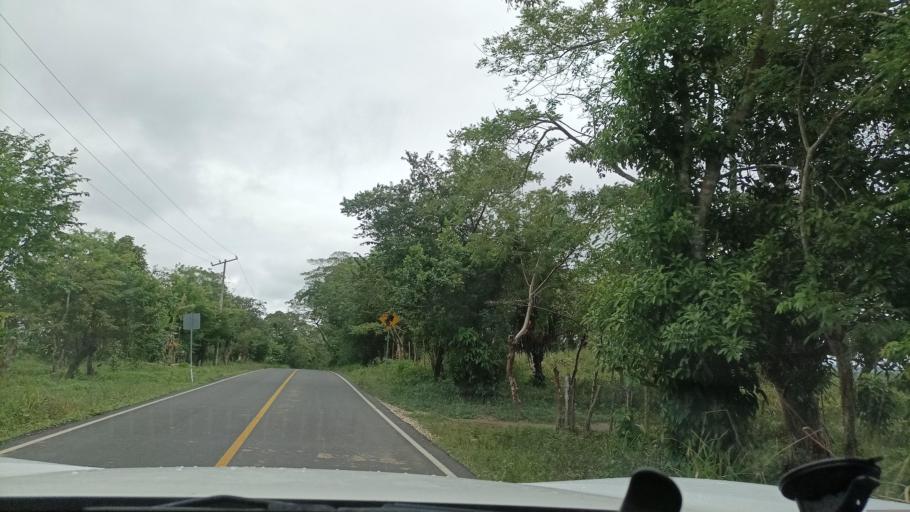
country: MX
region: Veracruz
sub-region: Moloacan
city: Cuichapa
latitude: 17.7982
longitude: -94.3581
